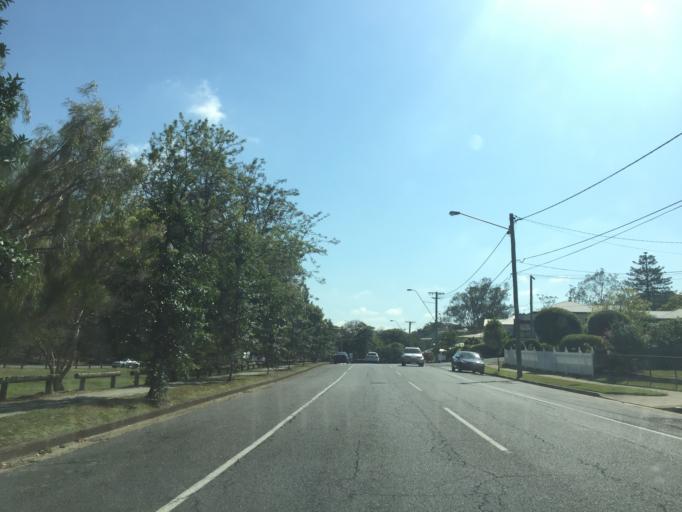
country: AU
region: Queensland
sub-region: Brisbane
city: Milton
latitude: -27.4660
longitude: 152.9906
